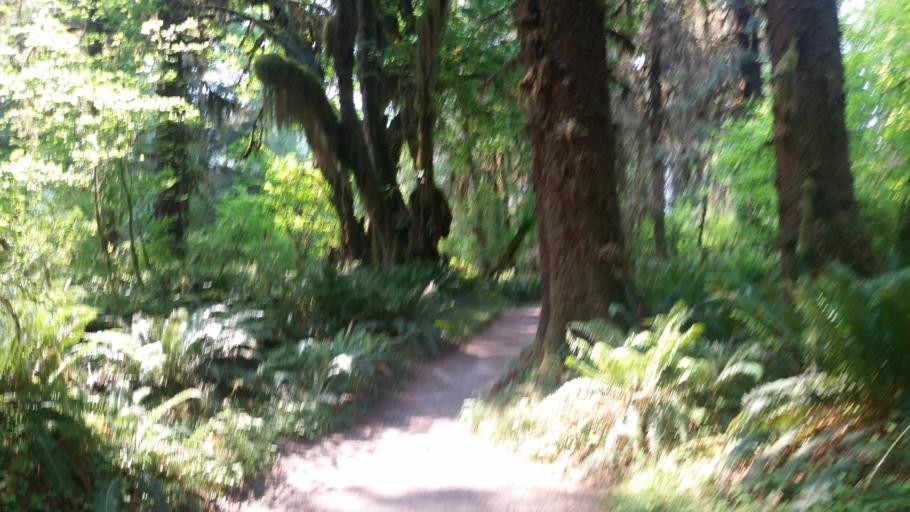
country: US
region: Washington
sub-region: Clallam County
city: Forks
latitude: 47.8577
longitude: -123.9292
